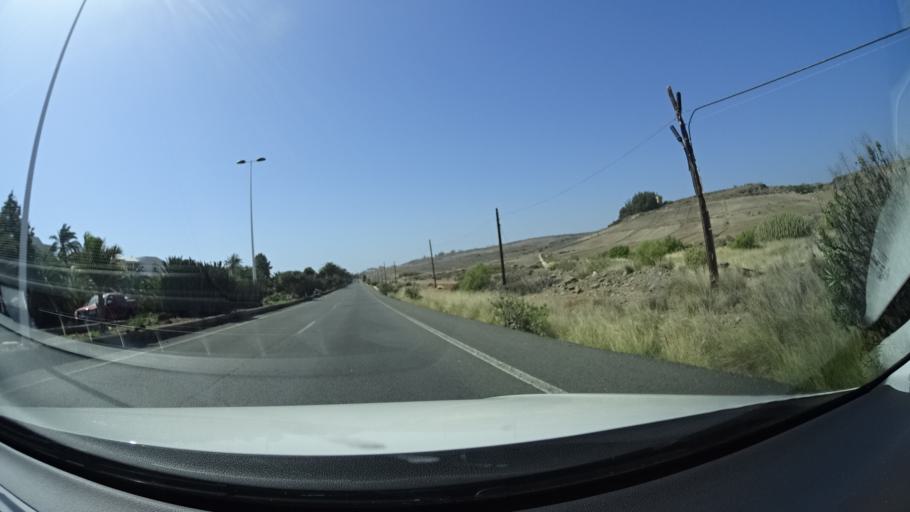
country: ES
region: Canary Islands
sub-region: Provincia de Las Palmas
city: Playa del Ingles
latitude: 27.7827
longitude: -15.5201
